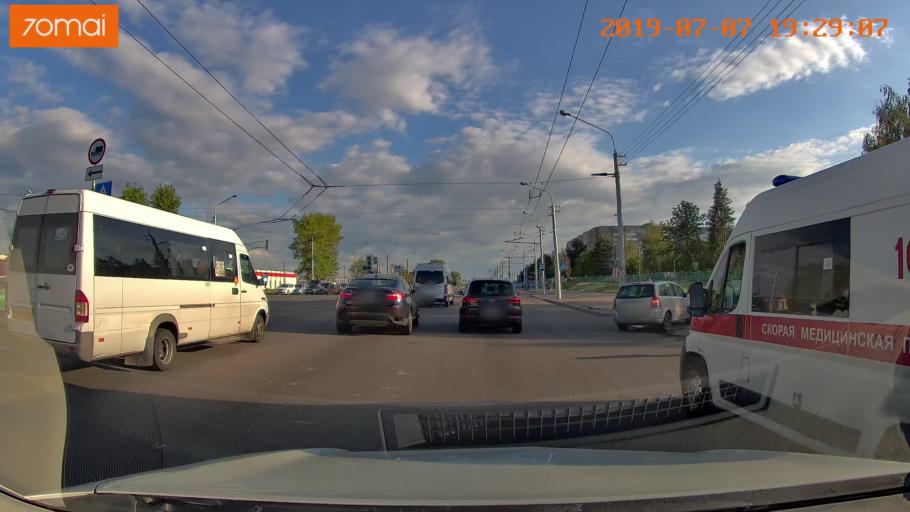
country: BY
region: Minsk
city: Syenitsa
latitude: 53.8506
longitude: 27.5369
